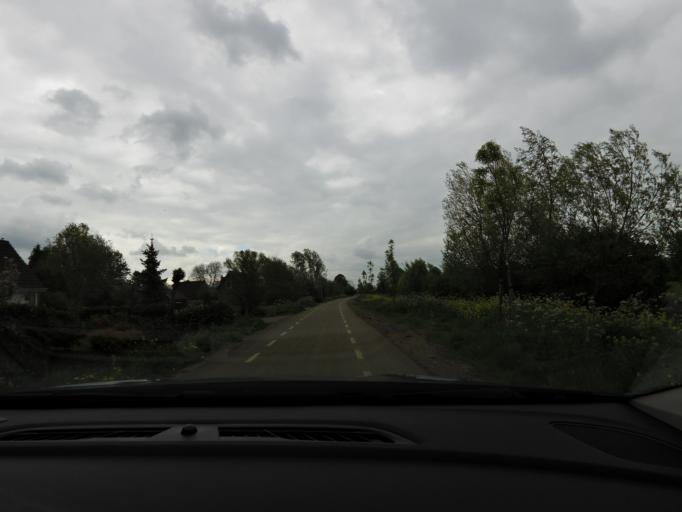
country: NL
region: North Brabant
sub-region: Gemeente Woudrichem
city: Woudrichem
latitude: 51.8566
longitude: 5.0203
